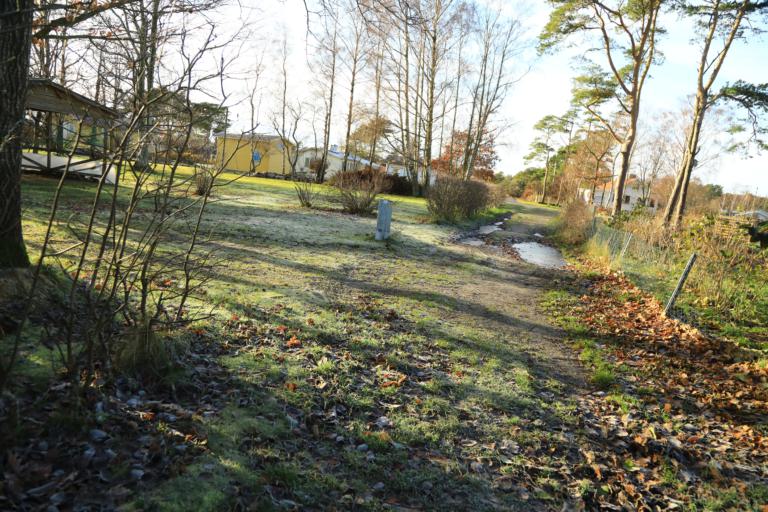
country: SE
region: Halland
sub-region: Varbergs Kommun
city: Varberg
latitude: 57.1913
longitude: 12.1850
